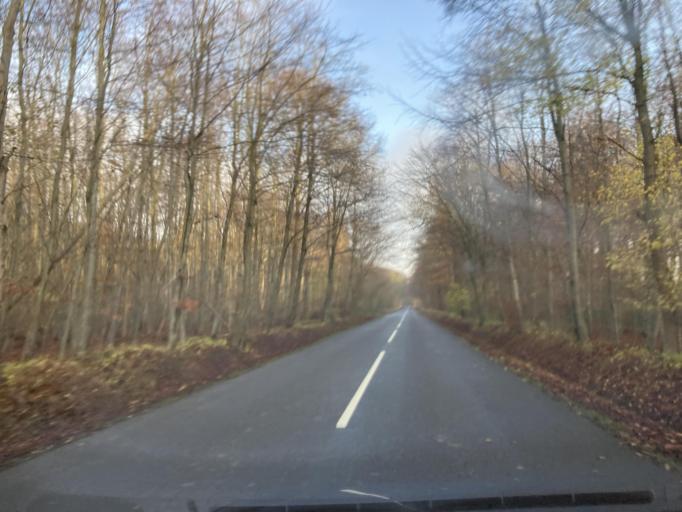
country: DK
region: Zealand
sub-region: Lolland Kommune
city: Rodby
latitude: 54.7691
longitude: 11.3623
